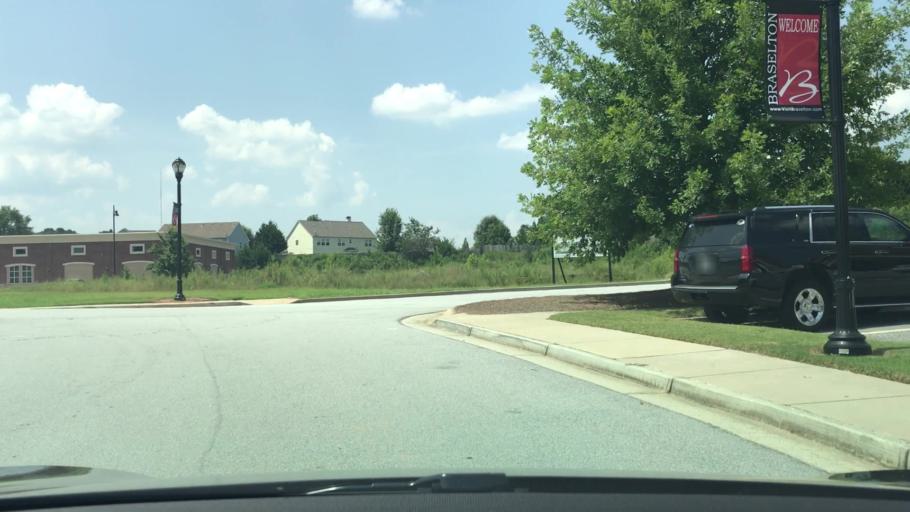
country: US
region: Georgia
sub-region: Jackson County
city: Braselton
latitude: 34.1146
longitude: -83.8190
